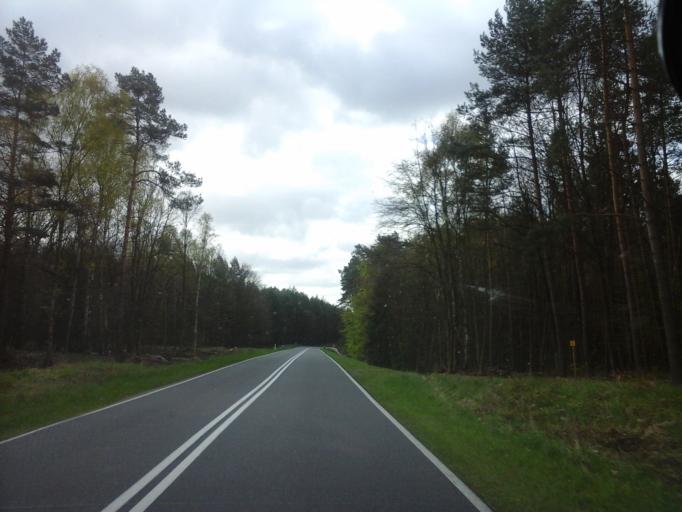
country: PL
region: West Pomeranian Voivodeship
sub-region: Powiat choszczenski
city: Bierzwnik
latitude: 53.0779
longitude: 15.6463
